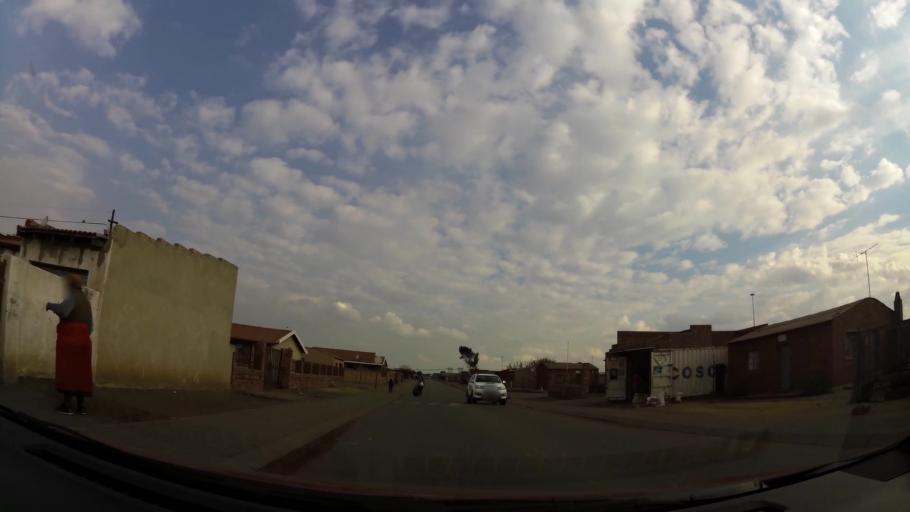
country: ZA
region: Gauteng
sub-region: Sedibeng District Municipality
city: Vanderbijlpark
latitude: -26.6928
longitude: 27.8751
